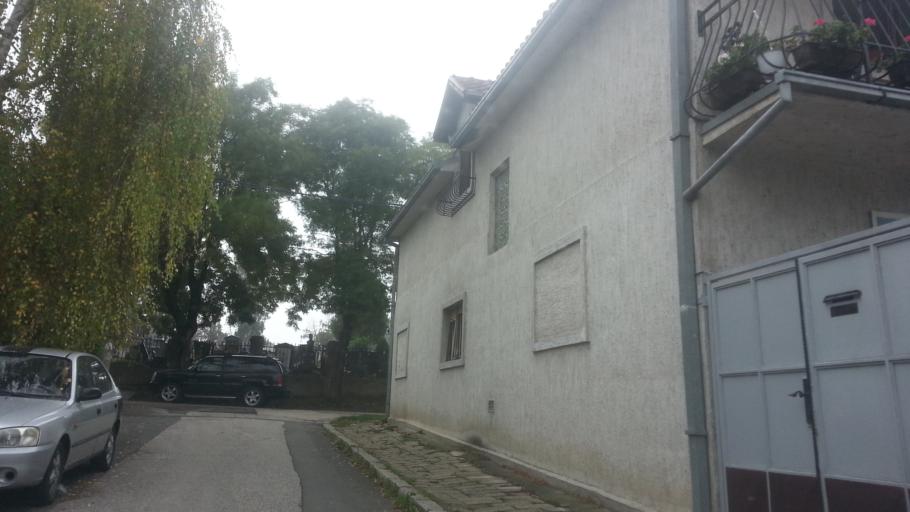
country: RS
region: Central Serbia
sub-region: Belgrade
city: Zemun
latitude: 44.8497
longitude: 20.4079
